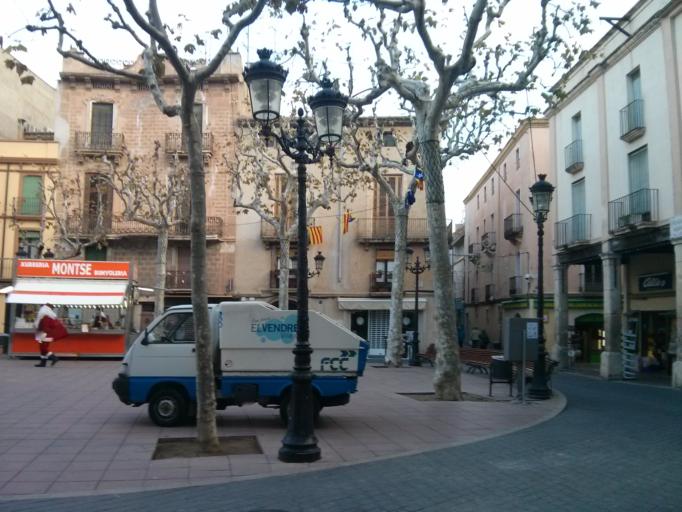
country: ES
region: Catalonia
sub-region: Provincia de Tarragona
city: El Vendrell
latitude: 41.2213
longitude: 1.5349
